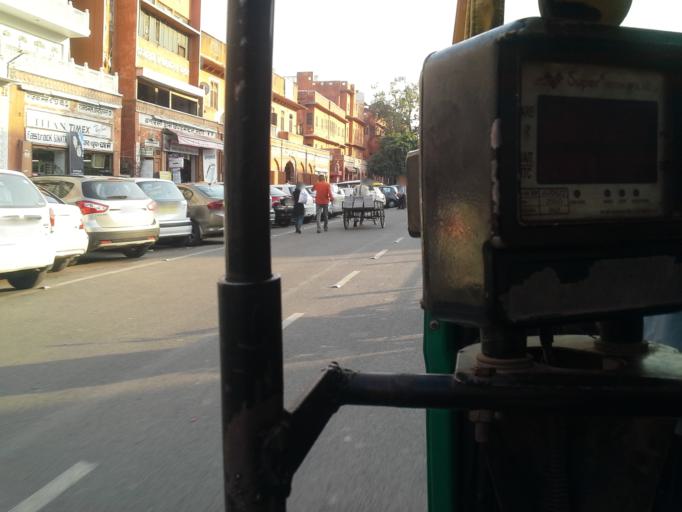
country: IN
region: Rajasthan
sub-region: Jaipur
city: Jaipur
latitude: 26.9194
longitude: 75.8215
